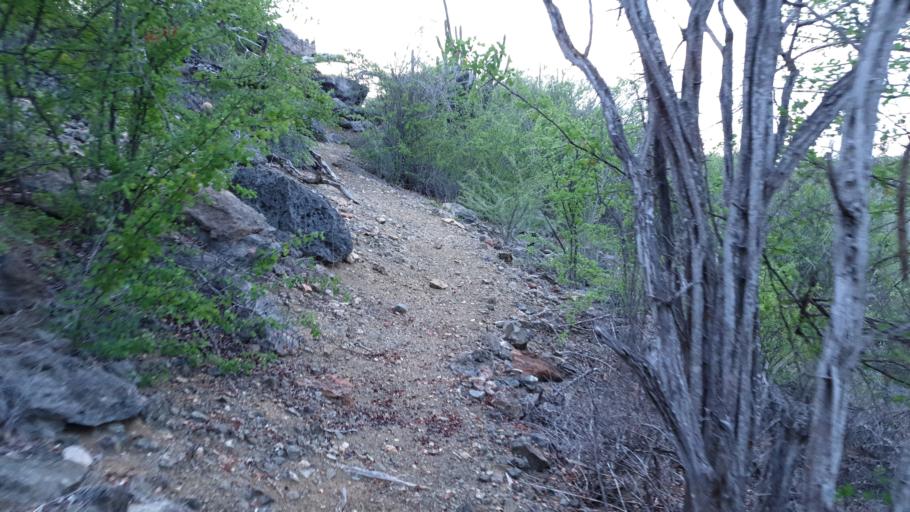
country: CW
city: Newport
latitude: 12.1292
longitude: -68.8142
